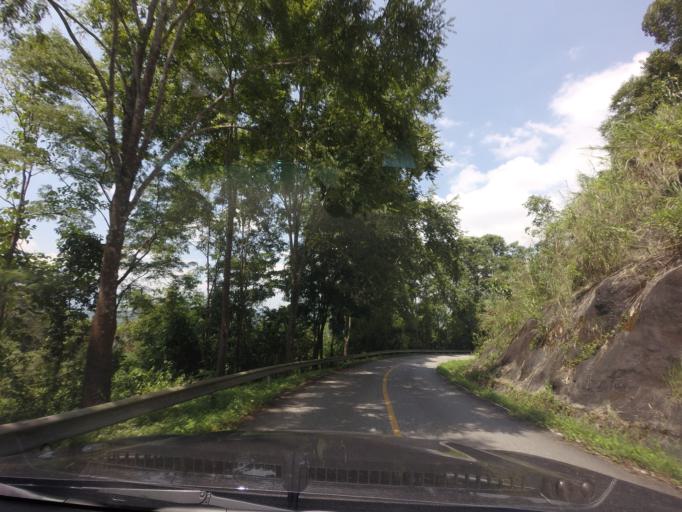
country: TH
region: Loei
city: Na Haeo
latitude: 17.6293
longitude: 100.9029
